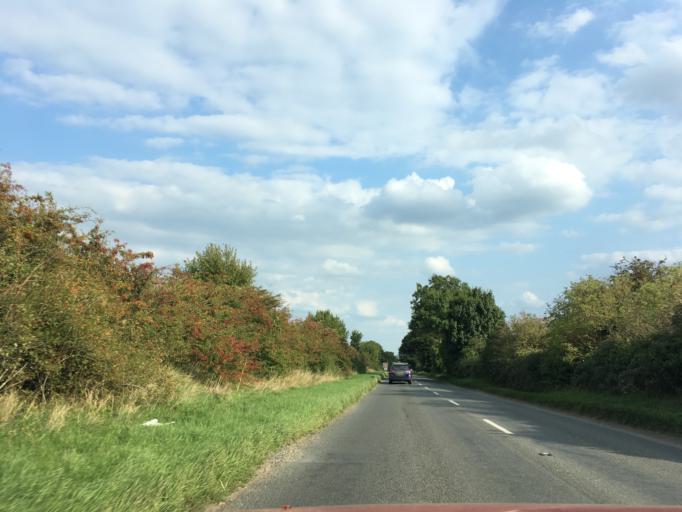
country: GB
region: England
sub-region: Gloucestershire
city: Nailsworth
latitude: 51.6507
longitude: -2.2295
